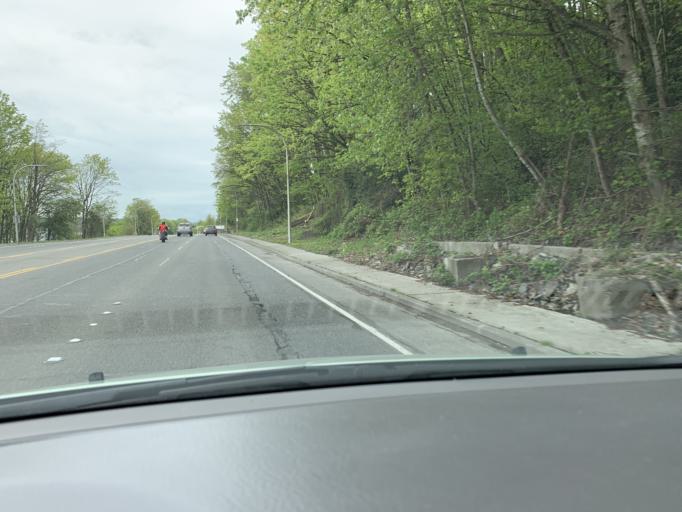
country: US
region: Washington
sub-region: King County
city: Renton
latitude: 47.4950
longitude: -122.2195
